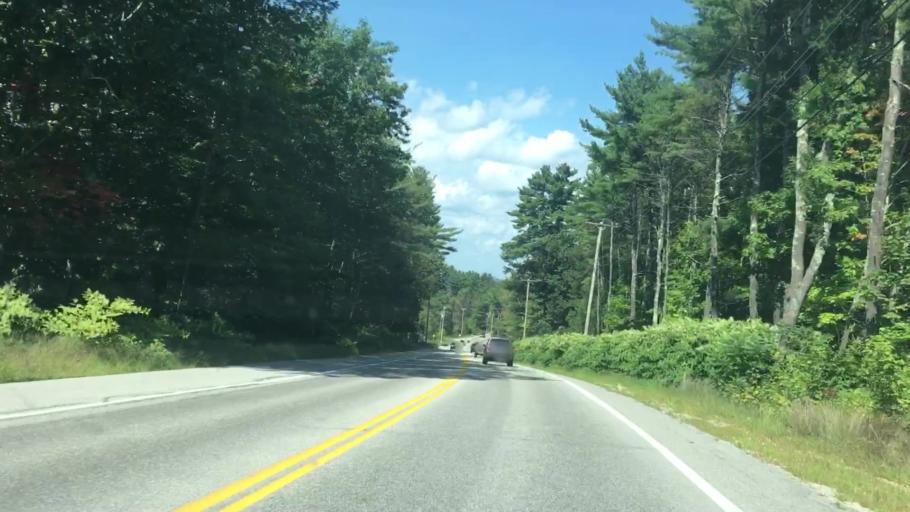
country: US
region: Maine
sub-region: Cumberland County
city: New Gloucester
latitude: 43.9049
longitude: -70.3234
